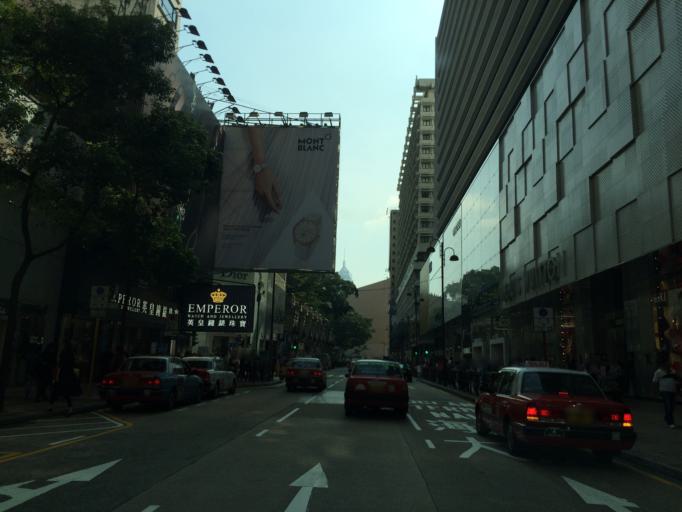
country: HK
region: Wanchai
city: Wan Chai
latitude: 22.2969
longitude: 114.1692
